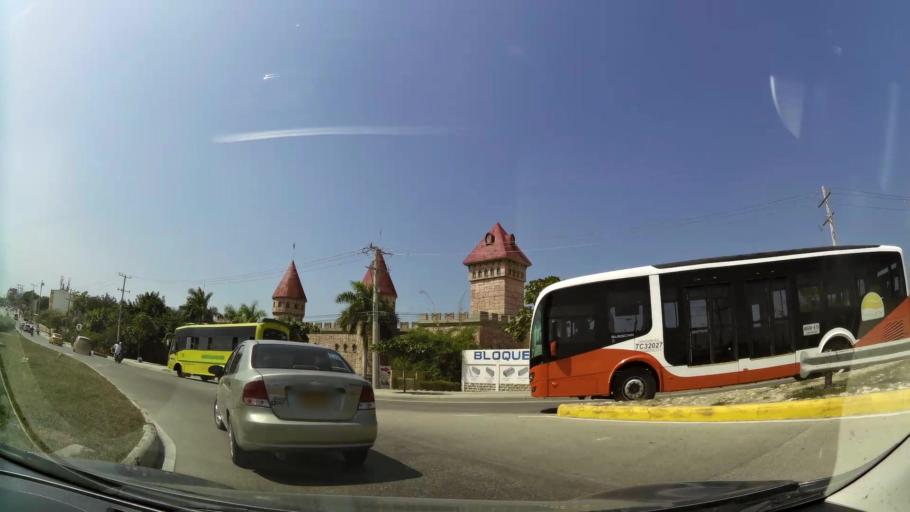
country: CO
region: Bolivar
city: Cartagena
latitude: 10.3976
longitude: -75.4727
